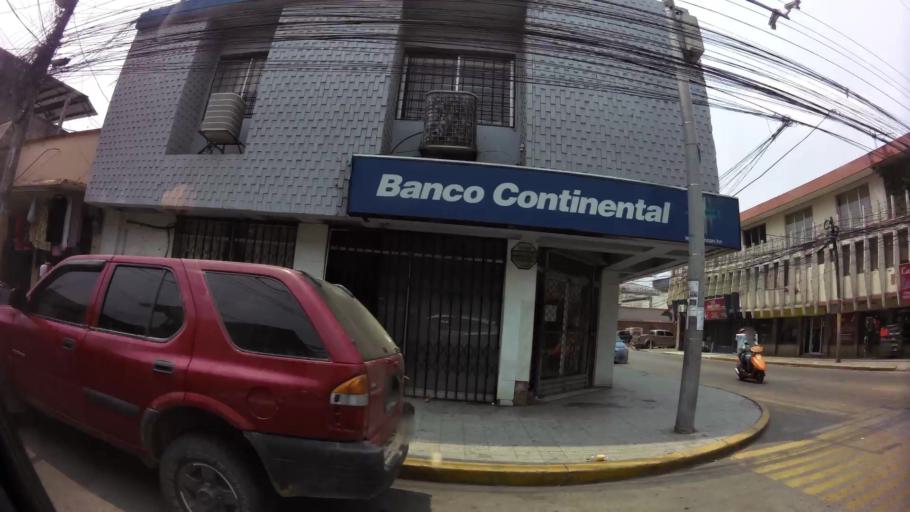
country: HN
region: Yoro
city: El Progreso
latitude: 15.4011
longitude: -87.8101
